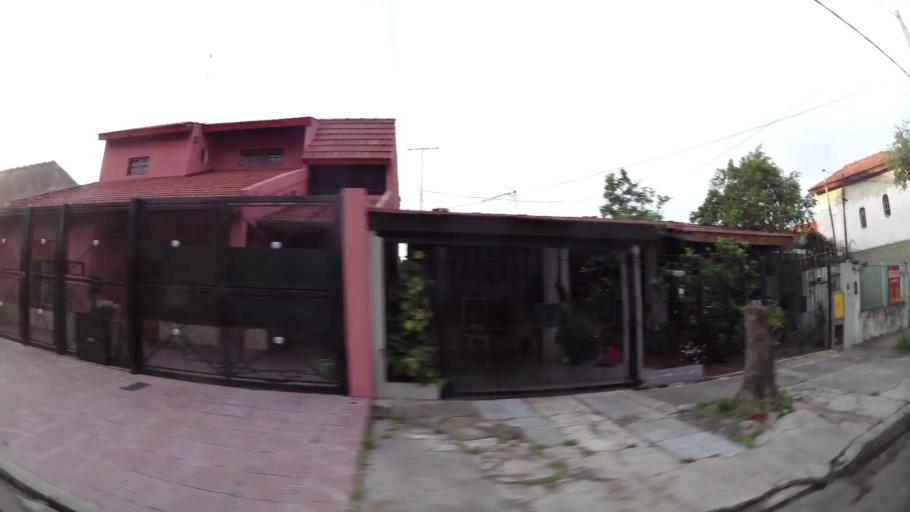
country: AR
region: Buenos Aires
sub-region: Partido de Almirante Brown
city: Adrogue
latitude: -34.7615
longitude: -58.3503
